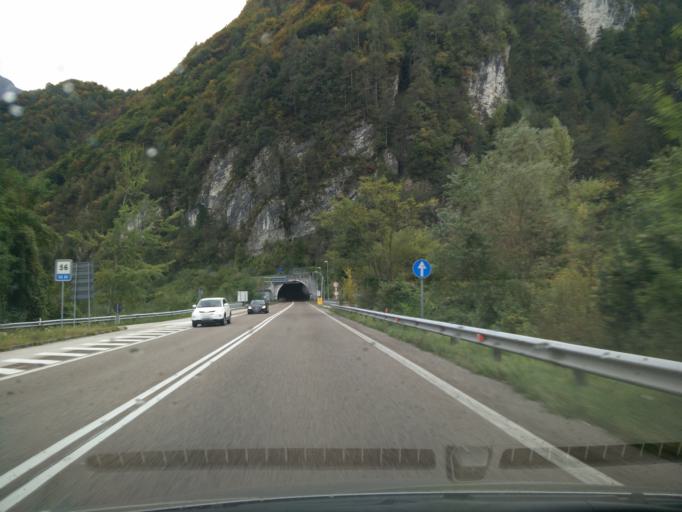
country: IT
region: Veneto
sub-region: Provincia di Belluno
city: Ospitale di Cadore
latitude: 46.3193
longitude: 12.3170
